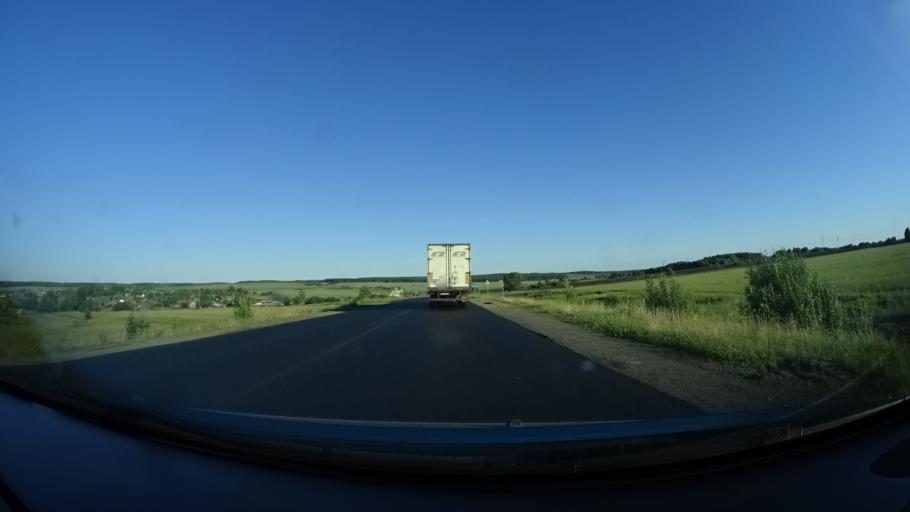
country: RU
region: Sverdlovsk
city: Achit
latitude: 56.8972
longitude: 57.6018
